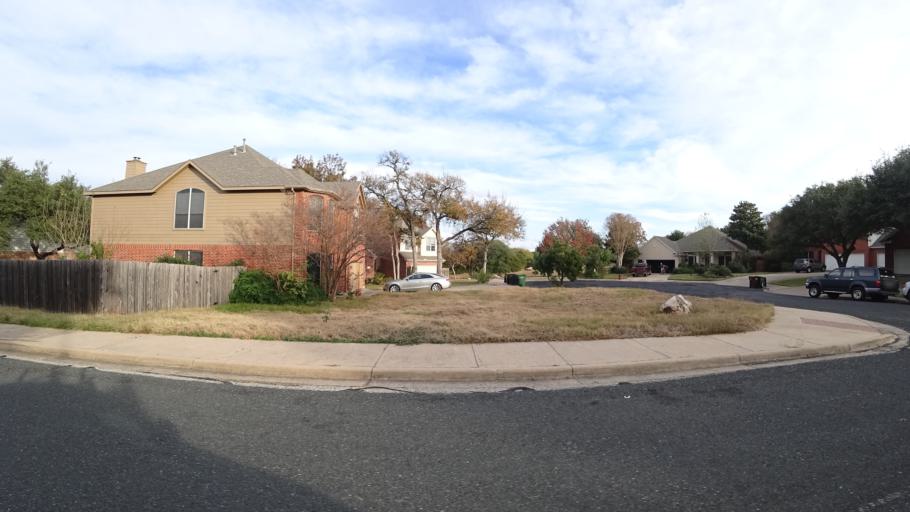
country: US
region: Texas
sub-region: Williamson County
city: Brushy Creek
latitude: 30.5173
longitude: -97.7232
